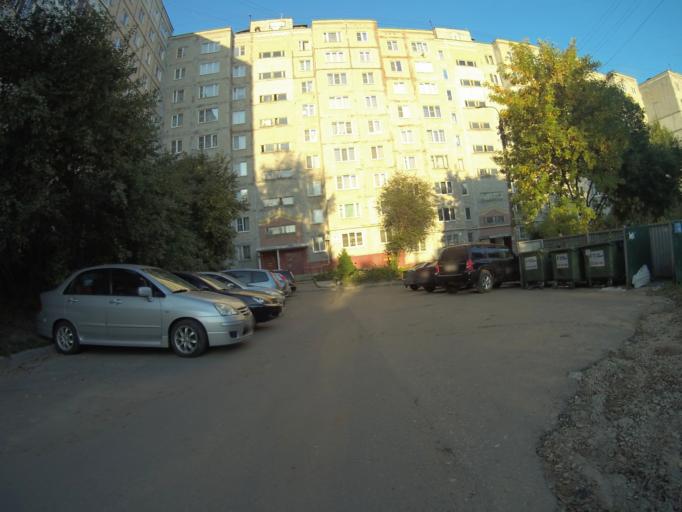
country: RU
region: Vladimir
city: Vladimir
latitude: 56.1083
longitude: 40.3542
